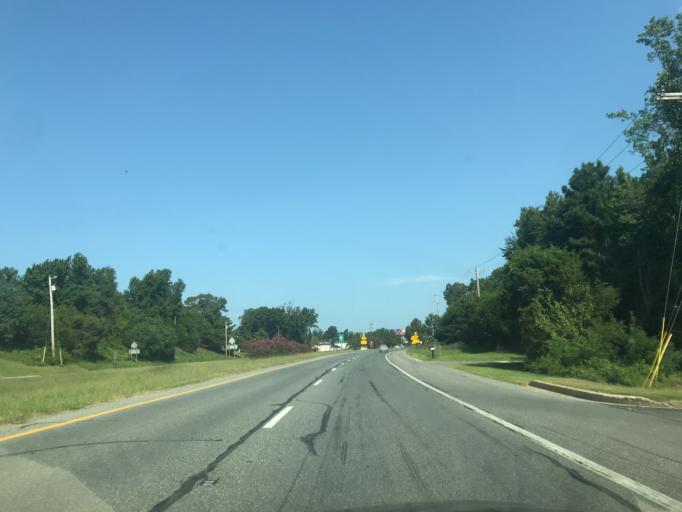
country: US
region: Maryland
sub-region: Saint Mary's County
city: Charlotte Hall
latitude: 38.4671
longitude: -76.7711
